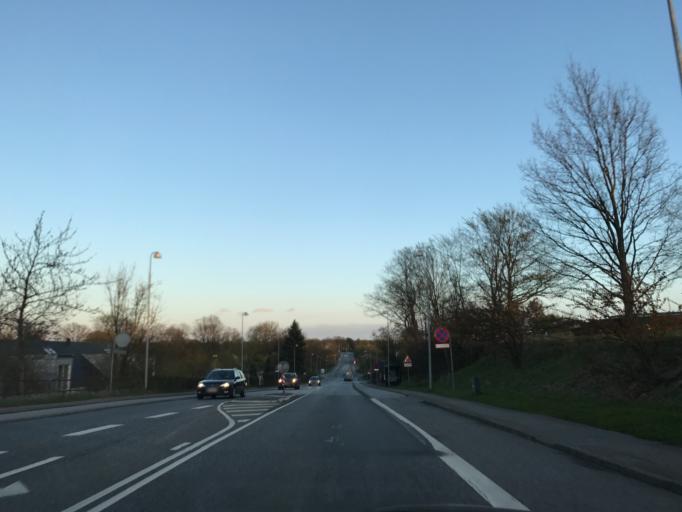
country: DK
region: Capital Region
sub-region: Fredensborg Kommune
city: Kokkedal
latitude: 55.8965
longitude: 12.4886
